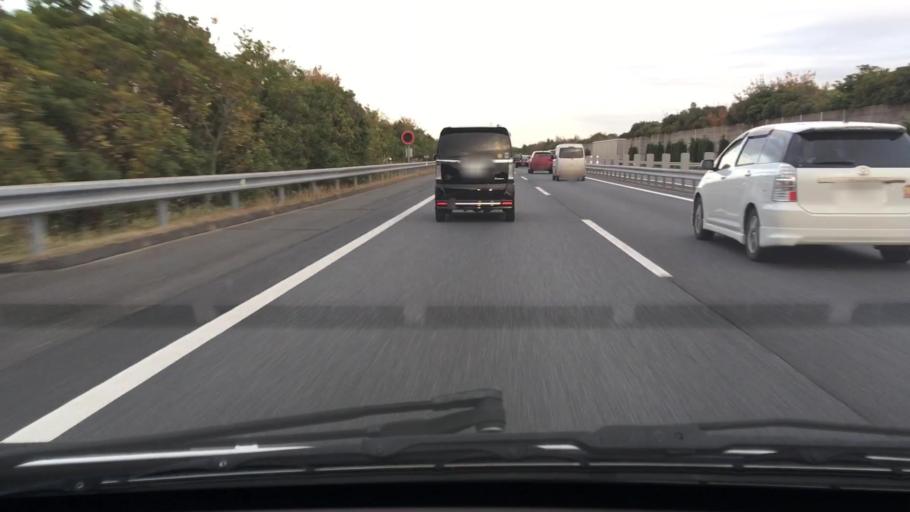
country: JP
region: Chiba
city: Ichihara
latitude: 35.5160
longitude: 140.1180
